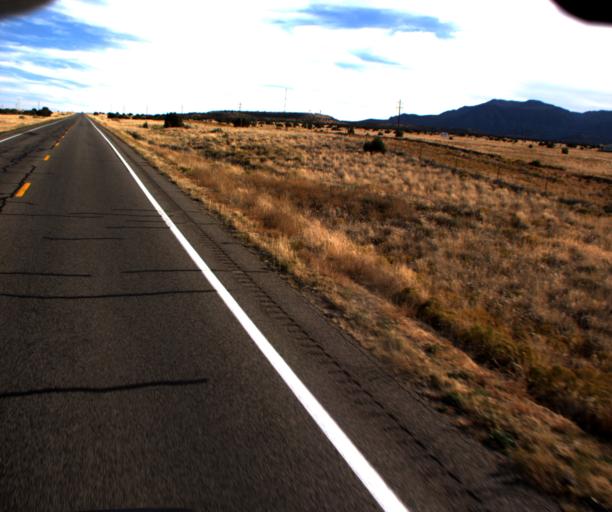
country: US
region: New Mexico
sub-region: San Juan County
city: Shiprock
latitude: 36.9023
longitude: -109.0680
